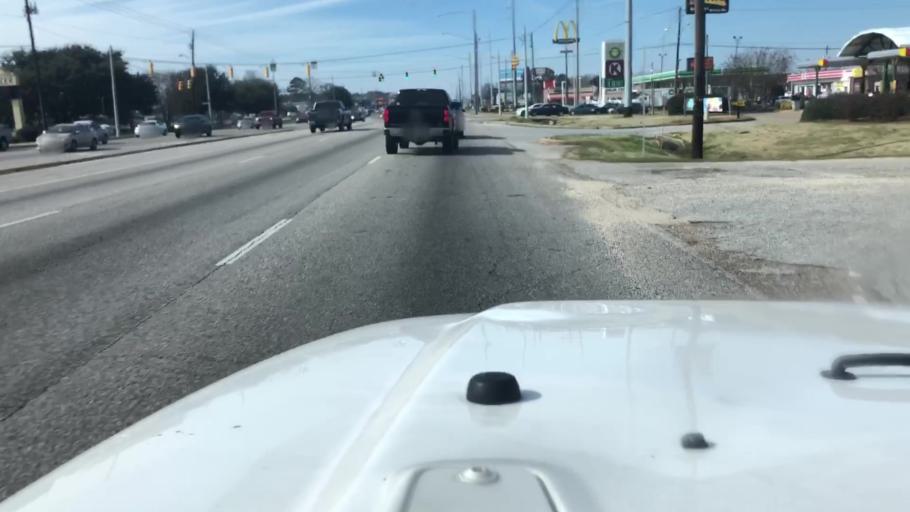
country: US
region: Alabama
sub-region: Montgomery County
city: Montgomery
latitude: 32.3823
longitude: -86.1982
